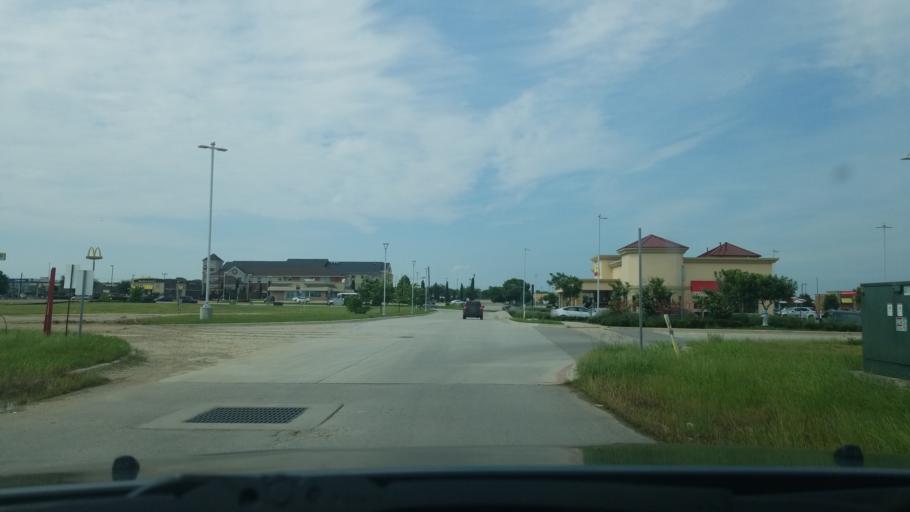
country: US
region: Texas
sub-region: Denton County
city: Denton
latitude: 33.2285
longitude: -97.1714
